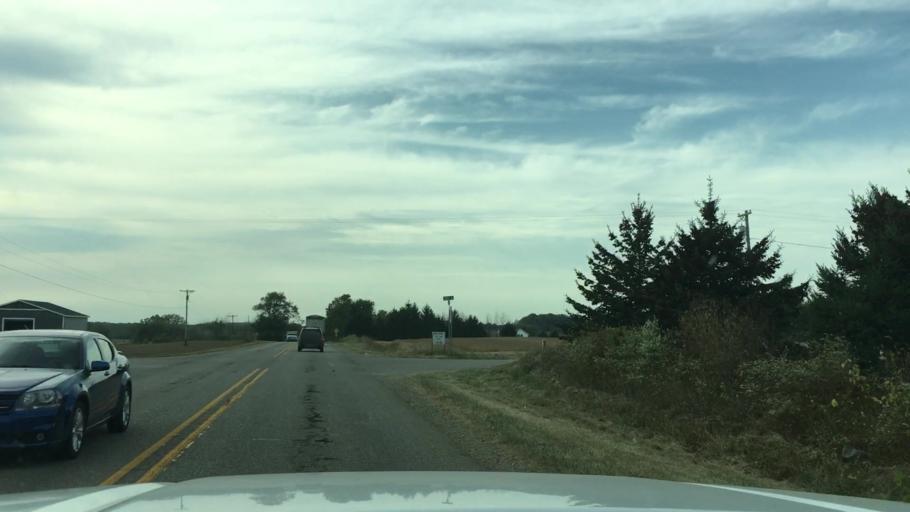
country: US
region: Michigan
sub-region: Ottawa County
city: Hudsonville
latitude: 42.7821
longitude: -85.8511
